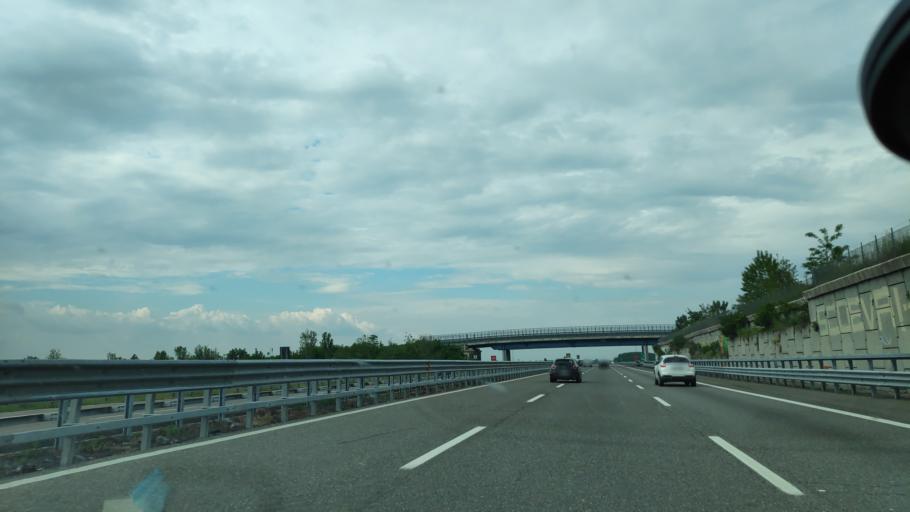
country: IT
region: Lombardy
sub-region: Provincia di Pavia
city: Silvano Pietra
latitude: 45.0444
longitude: 8.9451
